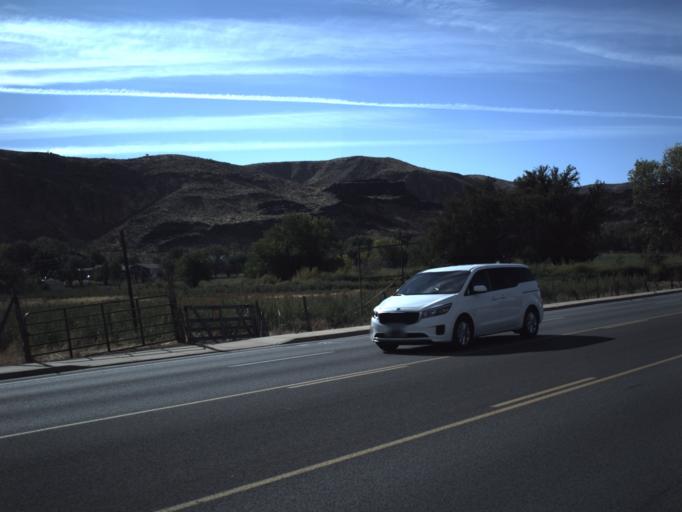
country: US
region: Utah
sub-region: Washington County
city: LaVerkin
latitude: 37.1987
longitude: -113.2738
